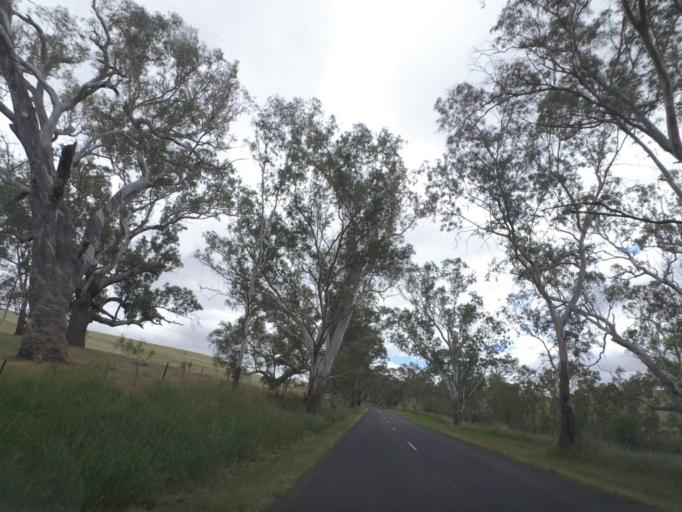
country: AU
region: Victoria
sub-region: Whittlesea
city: Whittlesea
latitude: -37.1947
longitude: 145.0382
